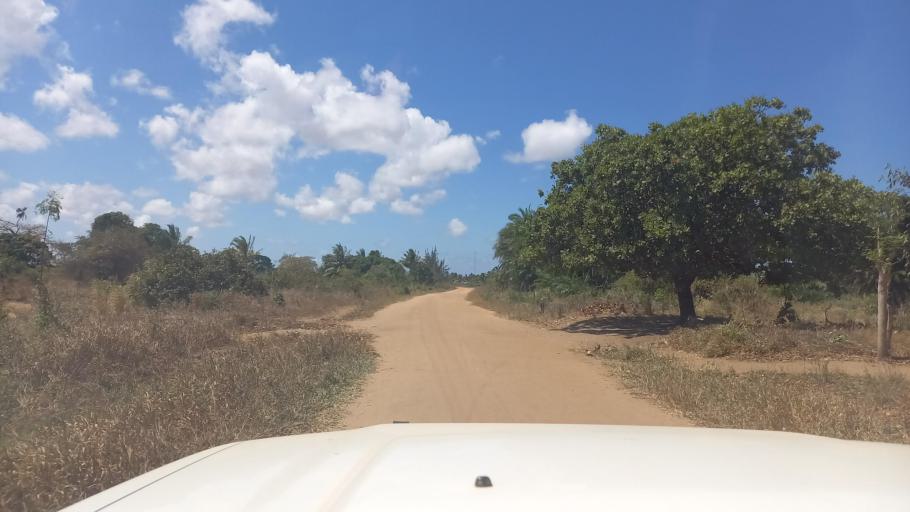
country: MZ
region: Cabo Delgado
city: Pemba
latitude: -13.4241
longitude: 40.5165
